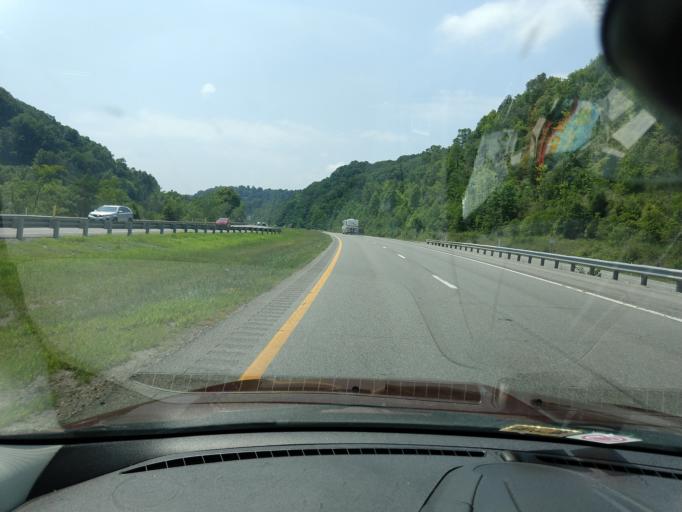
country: US
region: West Virginia
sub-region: Kanawha County
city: Sissonville
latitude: 38.5974
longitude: -81.6406
